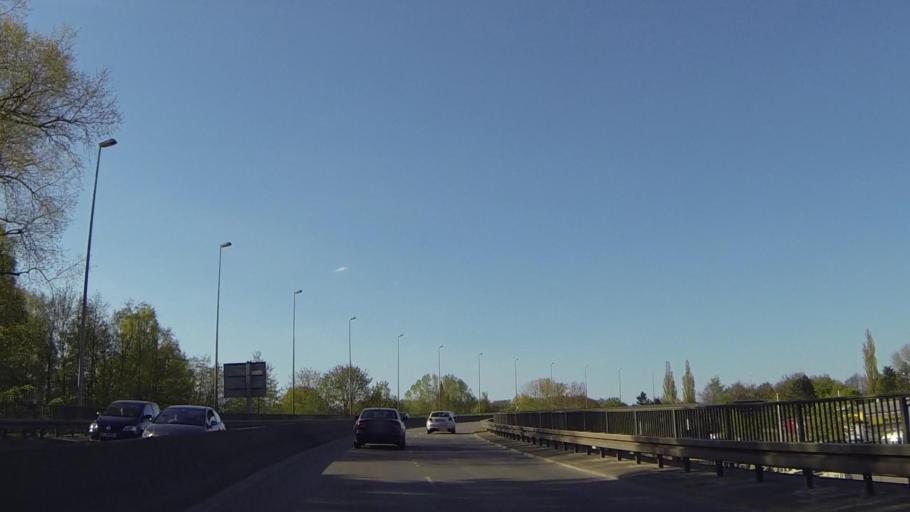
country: DE
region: Schleswig-Holstein
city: Pinneberg
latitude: 53.6598
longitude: 9.7865
